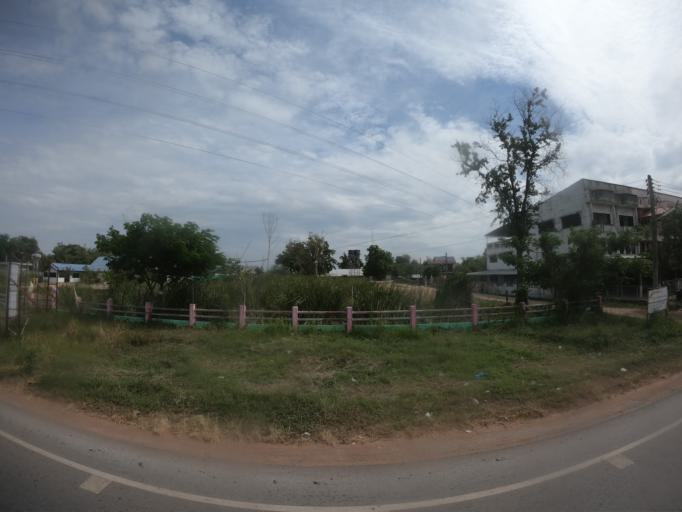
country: TH
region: Maha Sarakham
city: Chiang Yuen
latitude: 16.4015
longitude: 103.0997
